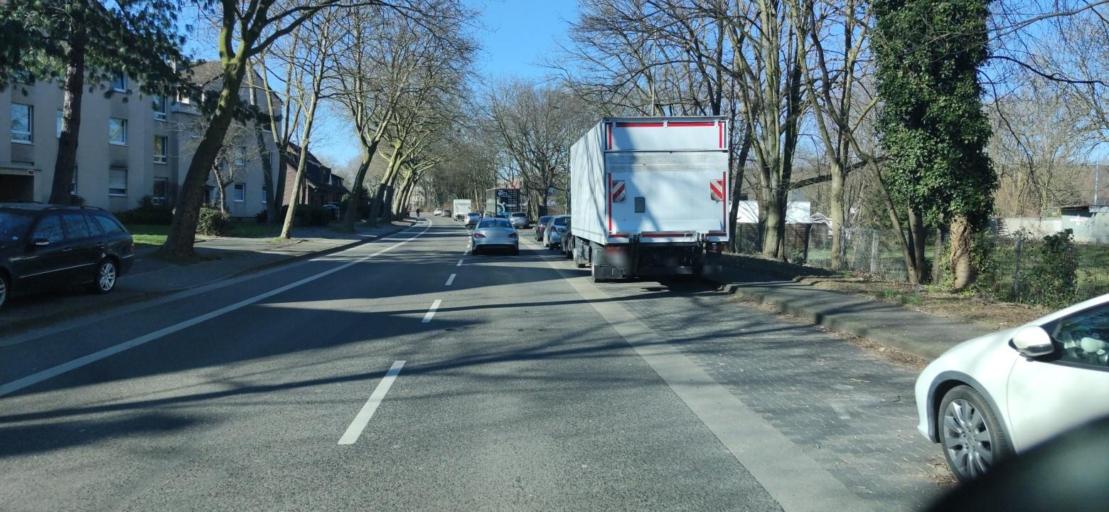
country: DE
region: North Rhine-Westphalia
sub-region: Regierungsbezirk Dusseldorf
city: Dinslaken
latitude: 51.5299
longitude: 6.7540
